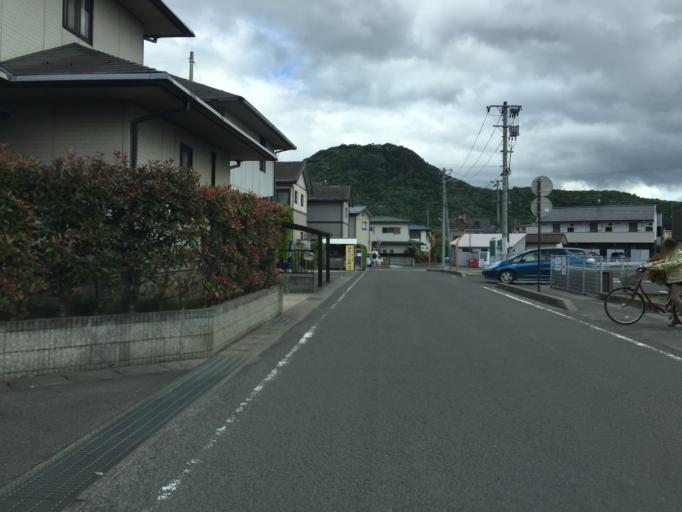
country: JP
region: Fukushima
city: Fukushima-shi
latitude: 37.7807
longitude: 140.4576
